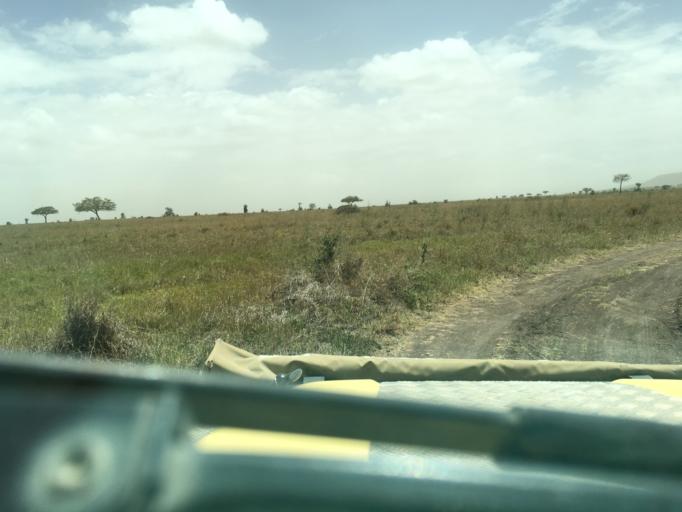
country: TZ
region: Simiyu
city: Kisesa
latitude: -2.7730
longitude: 34.7473
